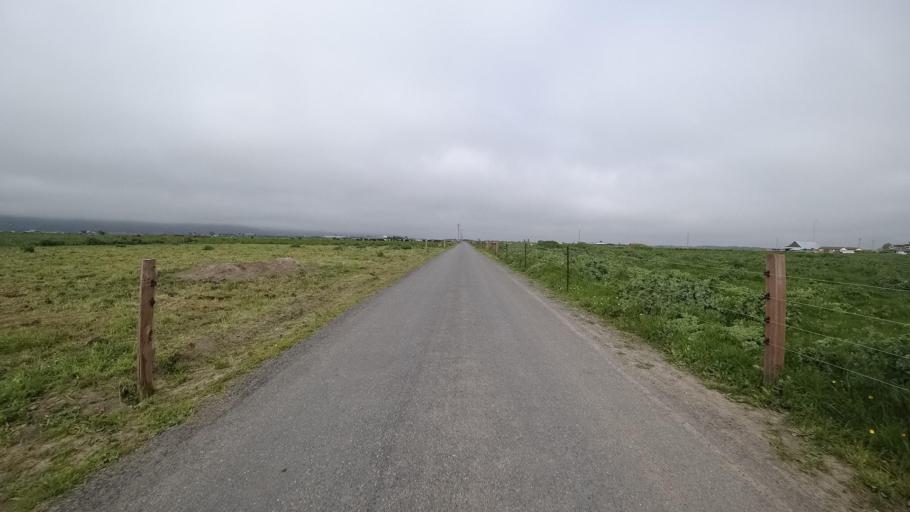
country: US
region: California
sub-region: Humboldt County
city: Fortuna
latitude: 40.5917
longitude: -124.1903
